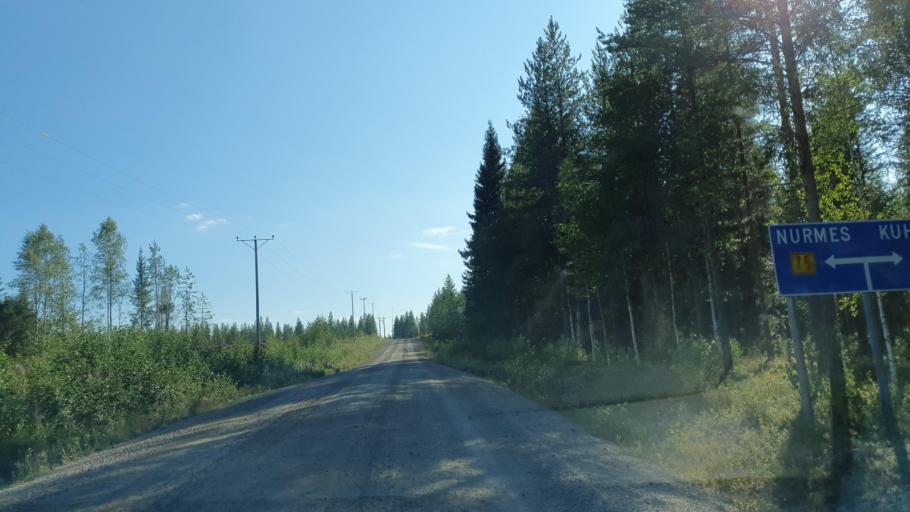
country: FI
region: Kainuu
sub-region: Kehys-Kainuu
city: Kuhmo
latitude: 64.0511
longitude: 29.5638
